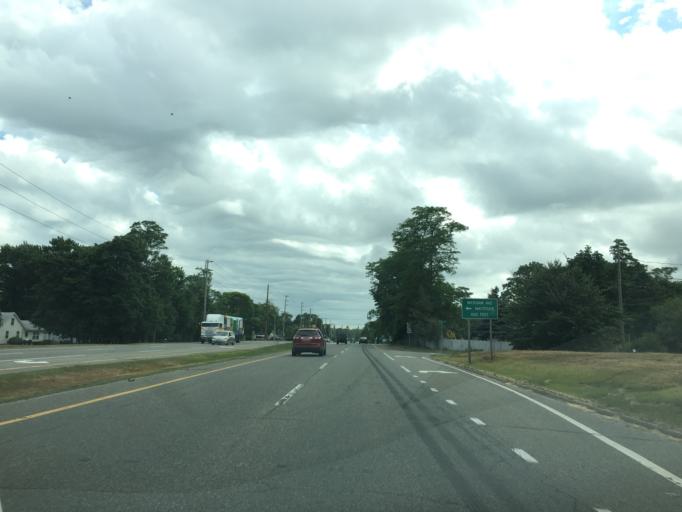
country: US
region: New York
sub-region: Suffolk County
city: Mattituck
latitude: 40.9966
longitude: -72.5329
